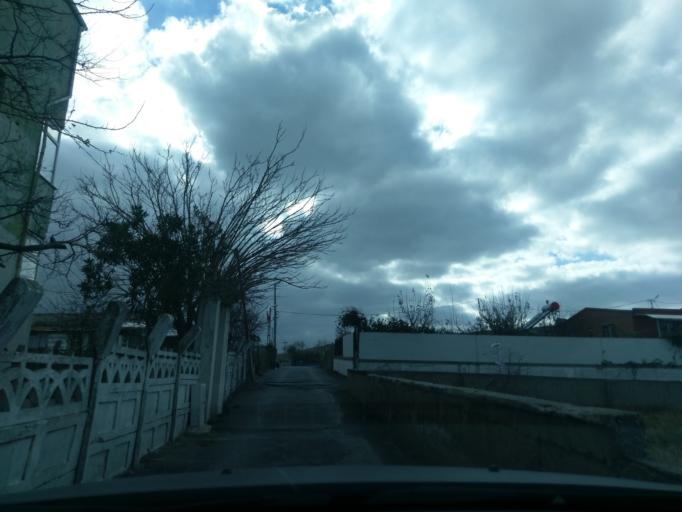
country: TR
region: Istanbul
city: Durusu
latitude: 41.3233
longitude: 28.7311
